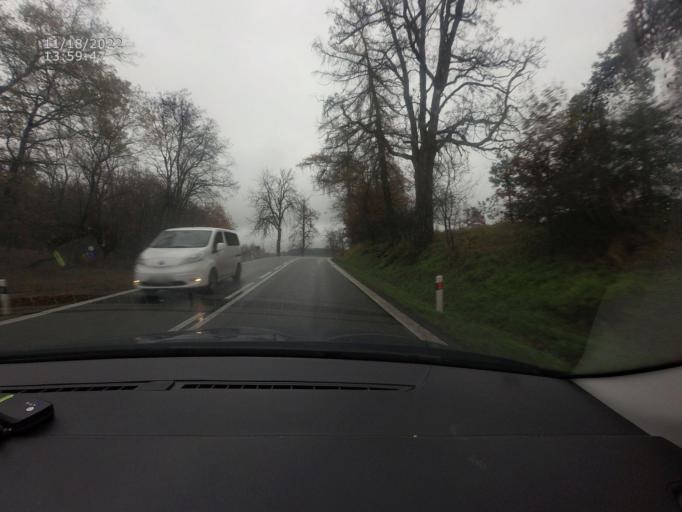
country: CZ
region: Jihocesky
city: Sedlice
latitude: 49.3559
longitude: 14.0055
